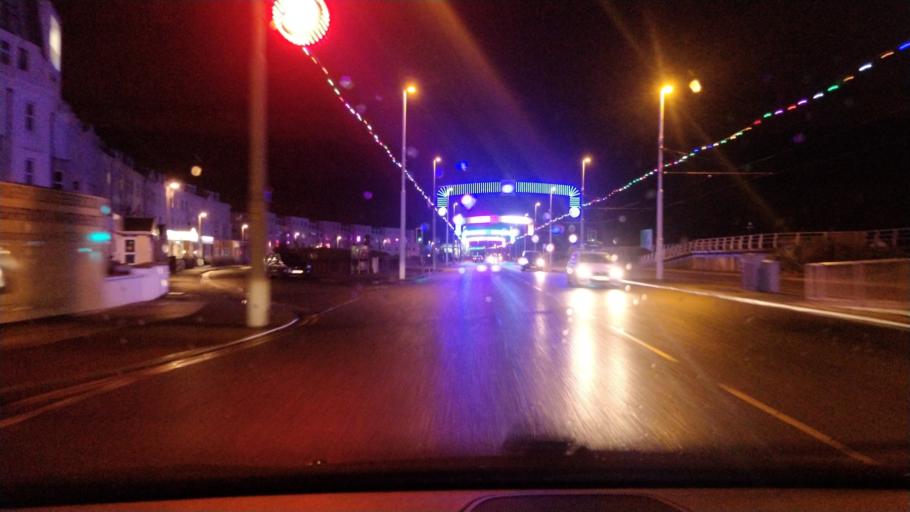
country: GB
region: England
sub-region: Blackpool
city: Blackpool
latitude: 53.7825
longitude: -3.0578
